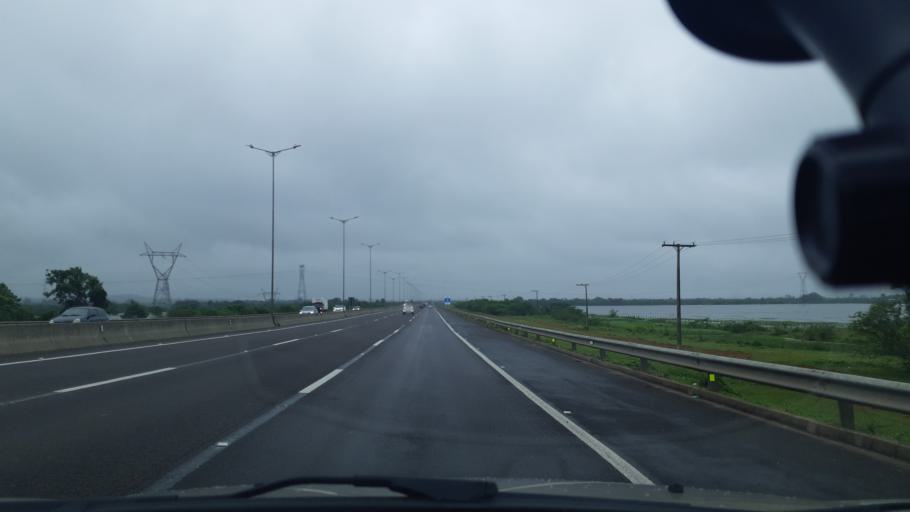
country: BR
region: Rio Grande do Sul
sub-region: Canoas
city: Canoas
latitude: -29.9034
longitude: -51.2449
